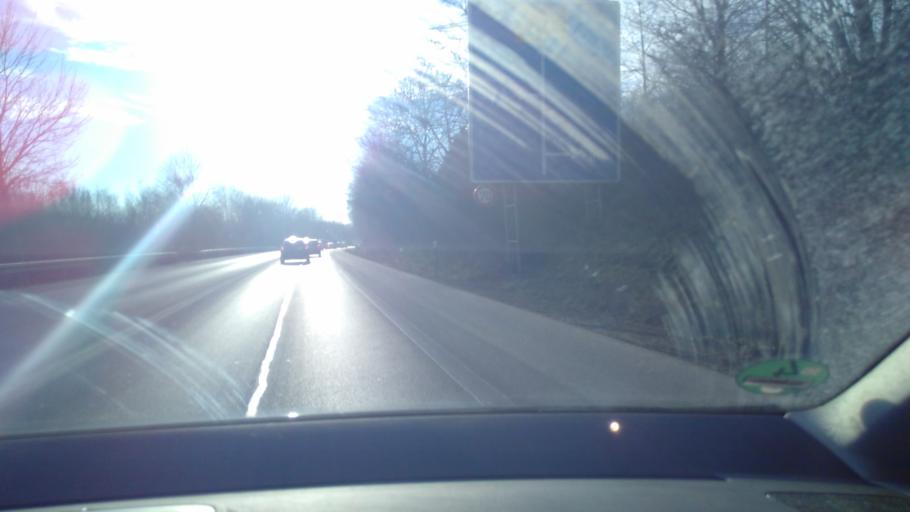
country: DE
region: North Rhine-Westphalia
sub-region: Regierungsbezirk Koln
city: Bergheim
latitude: 50.9512
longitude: 6.6076
